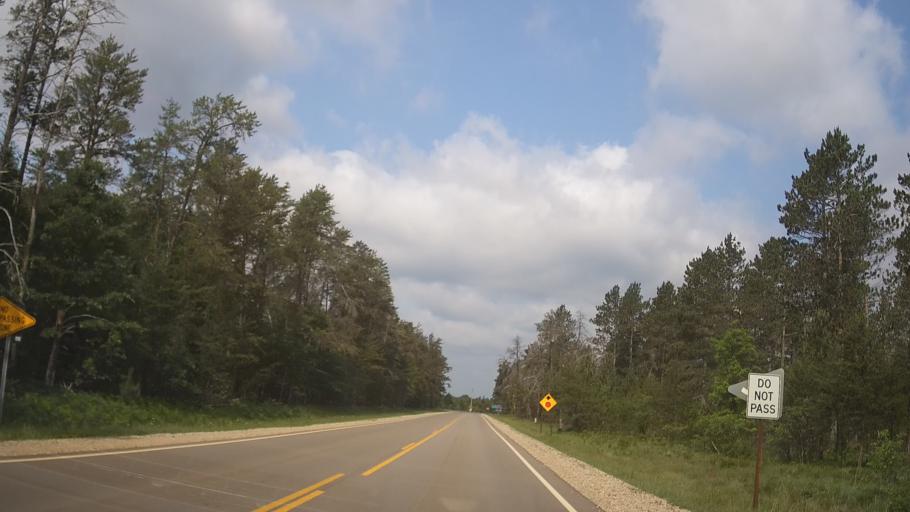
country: US
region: Michigan
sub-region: Roscommon County
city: Saint Helen
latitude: 44.4071
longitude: -84.4064
